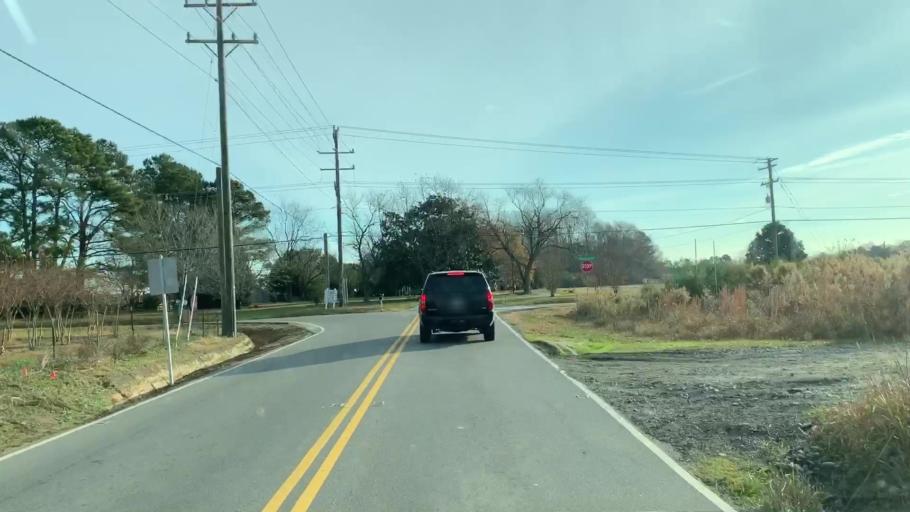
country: US
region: Virginia
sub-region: City of Virginia Beach
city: Virginia Beach
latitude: 36.6908
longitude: -76.0259
